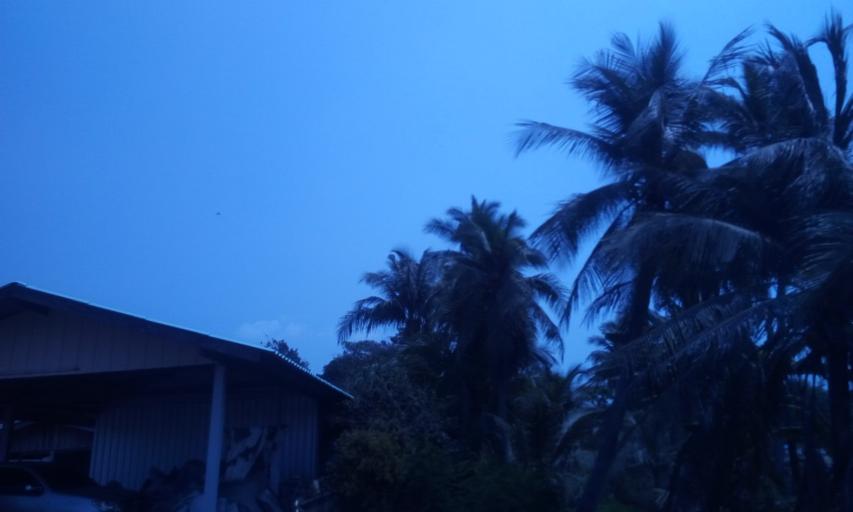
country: TH
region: Chachoengsao
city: Bang Nam Priao
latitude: 13.8775
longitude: 100.9678
